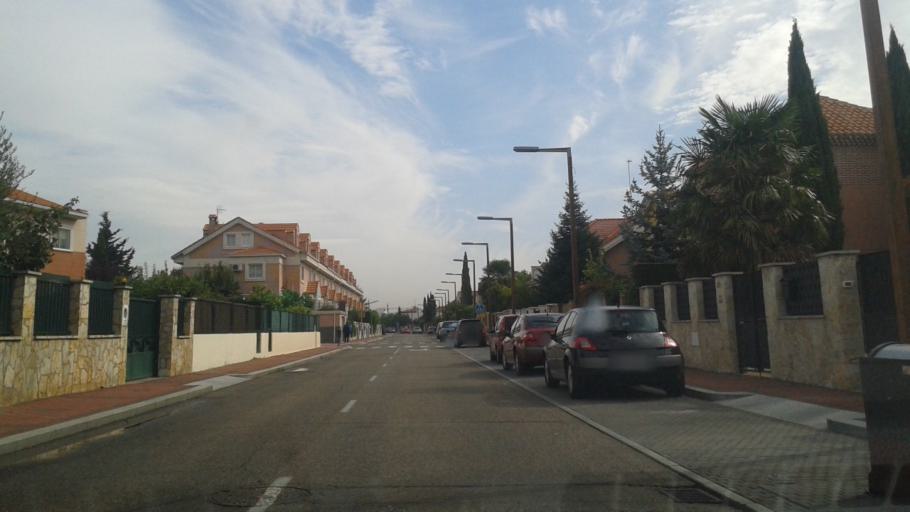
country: ES
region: Castille and Leon
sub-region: Provincia de Valladolid
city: Arroyo
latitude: 41.6098
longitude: -4.7893
